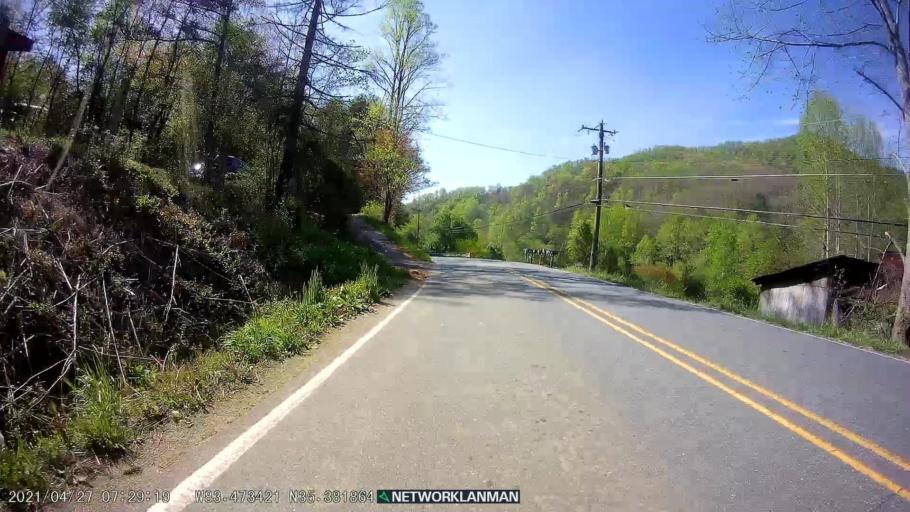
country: US
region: North Carolina
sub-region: Swain County
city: Bryson City
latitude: 35.3821
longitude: -83.4735
